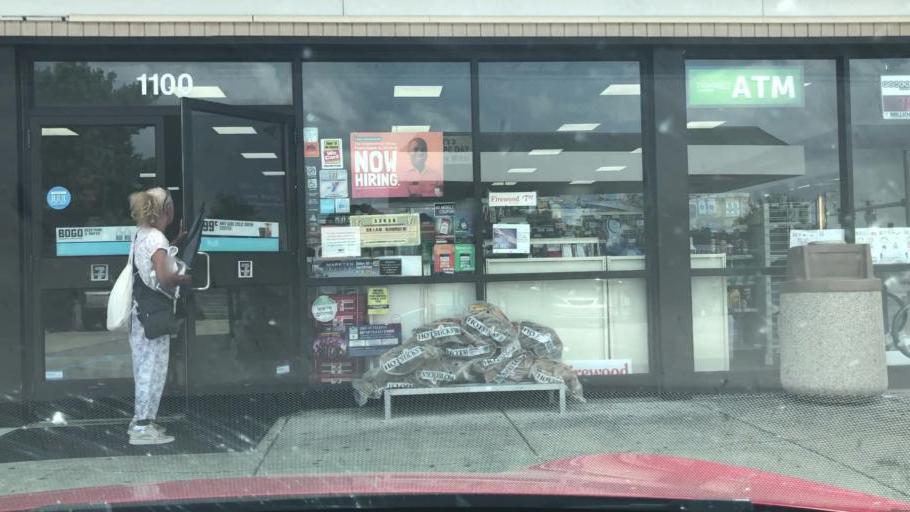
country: US
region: Virginia
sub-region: City of Chesapeake
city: Chesapeake
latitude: 36.8758
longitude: -76.1340
